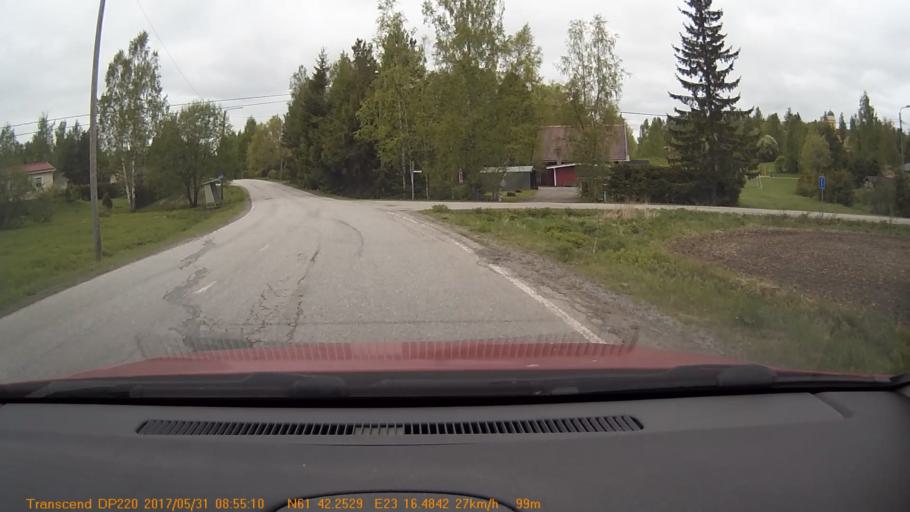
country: FI
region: Pirkanmaa
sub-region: Tampere
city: Viljakkala
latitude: 61.7041
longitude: 23.2749
